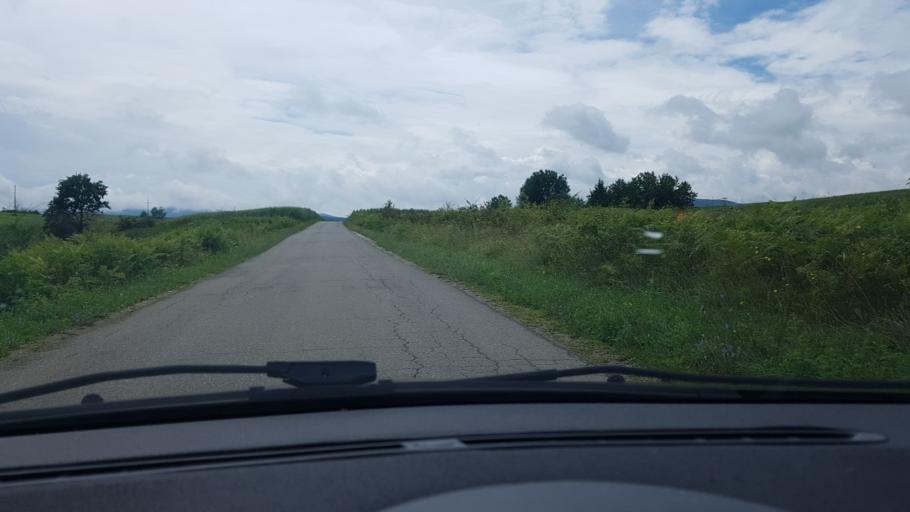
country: HR
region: Licko-Senjska
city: Jezerce
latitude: 44.9601
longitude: 15.6841
